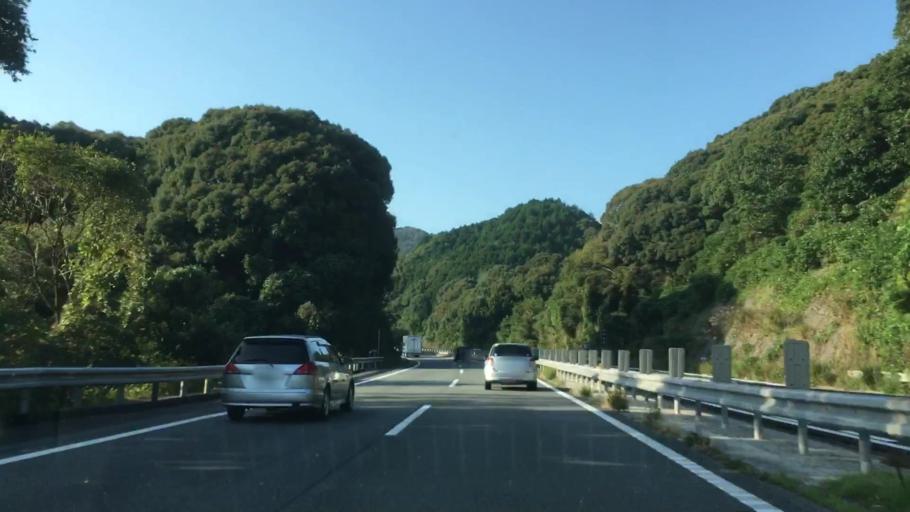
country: JP
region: Yamaguchi
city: Ogori-shimogo
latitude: 34.1328
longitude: 131.3762
